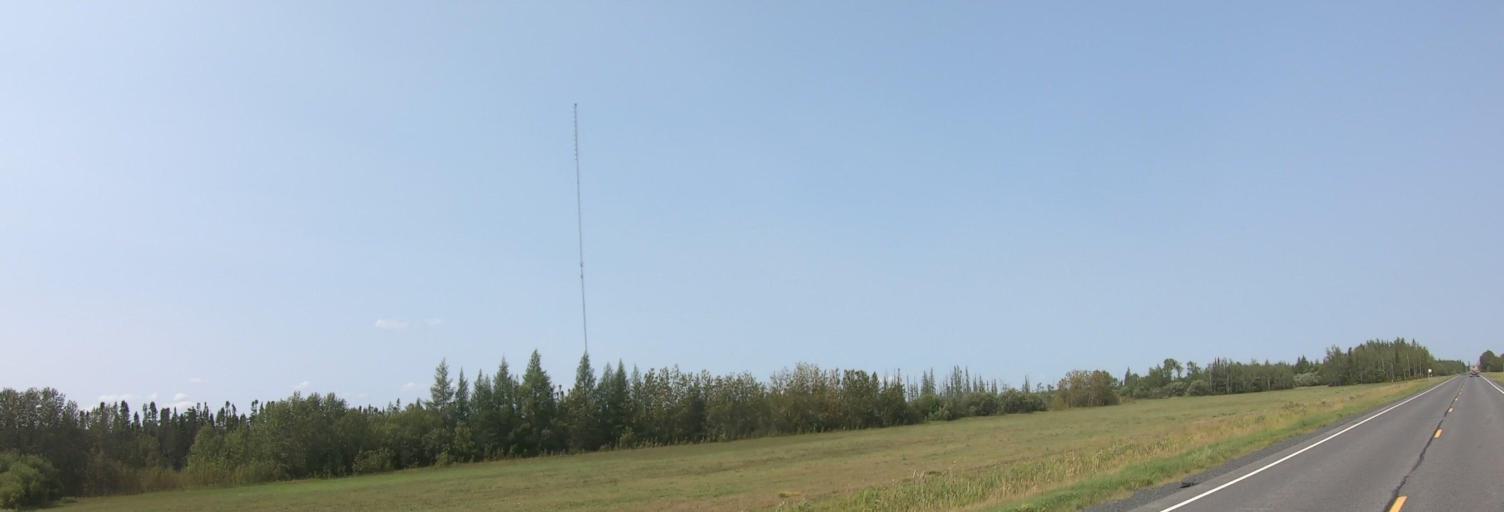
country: US
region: Minnesota
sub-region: Koochiching County
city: International Falls
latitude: 48.5603
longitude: -93.8182
